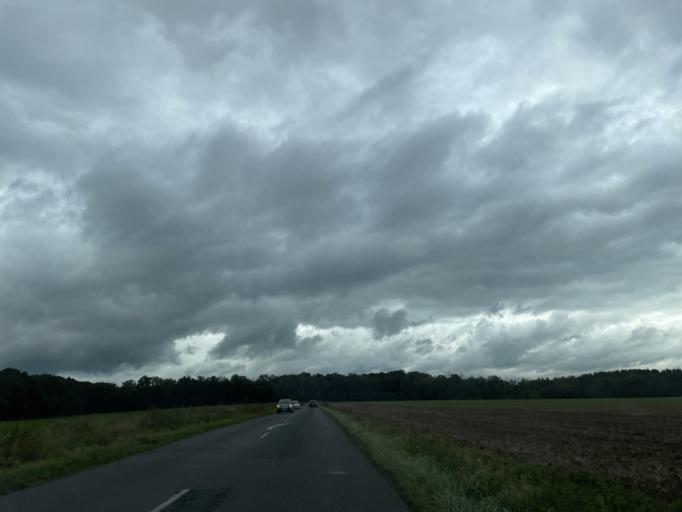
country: FR
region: Ile-de-France
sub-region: Departement de Seine-et-Marne
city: Sammeron
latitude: 48.8889
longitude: 3.0669
